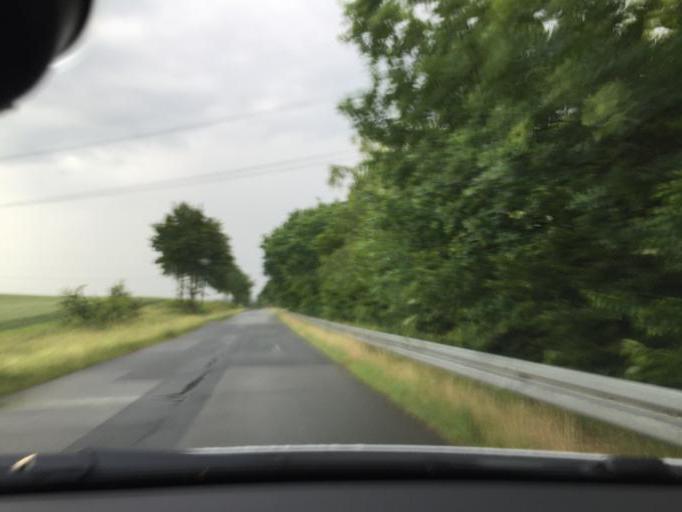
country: DE
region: Lower Saxony
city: Hehlen
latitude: 52.0307
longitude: 9.4072
